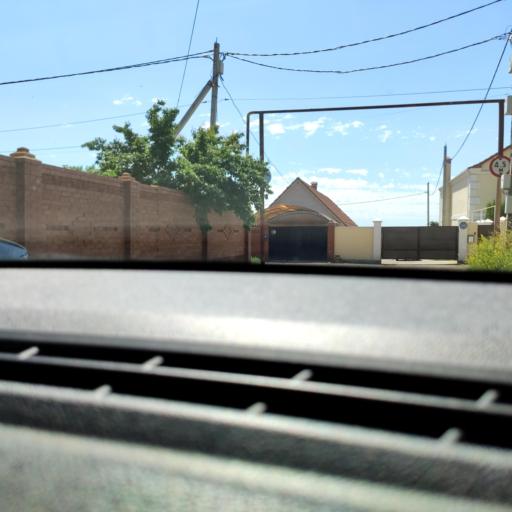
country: RU
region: Samara
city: Podstepki
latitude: 53.5077
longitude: 49.2389
